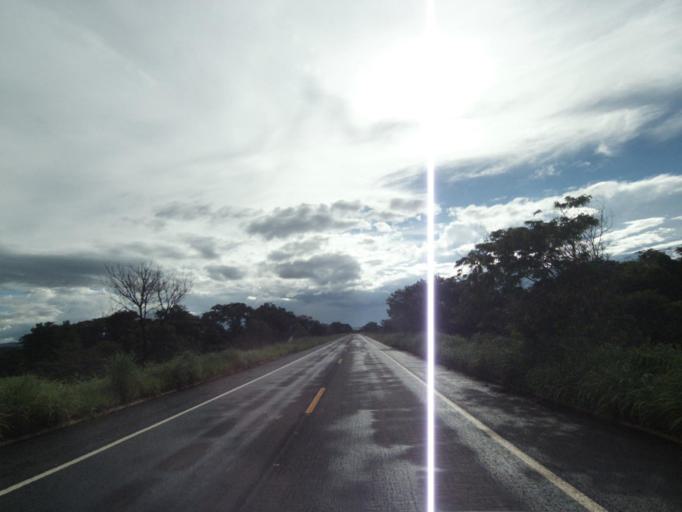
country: BR
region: Goias
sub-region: Itaberai
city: Itaberai
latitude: -15.9103
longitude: -49.5787
